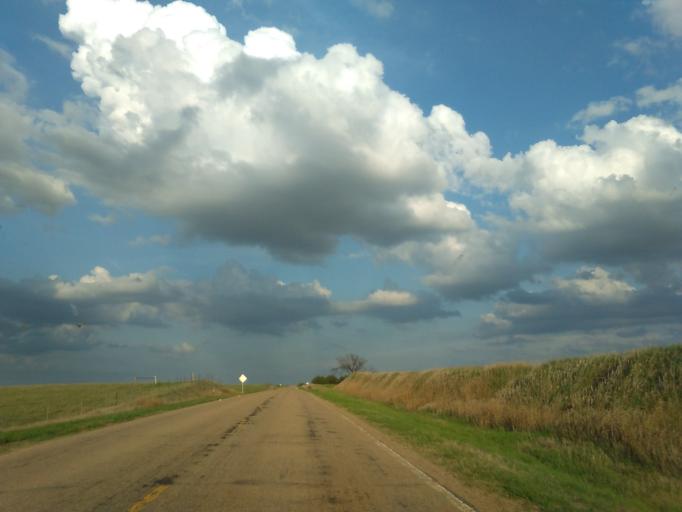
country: US
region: Nebraska
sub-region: Webster County
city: Red Cloud
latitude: 40.1759
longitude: -98.5150
